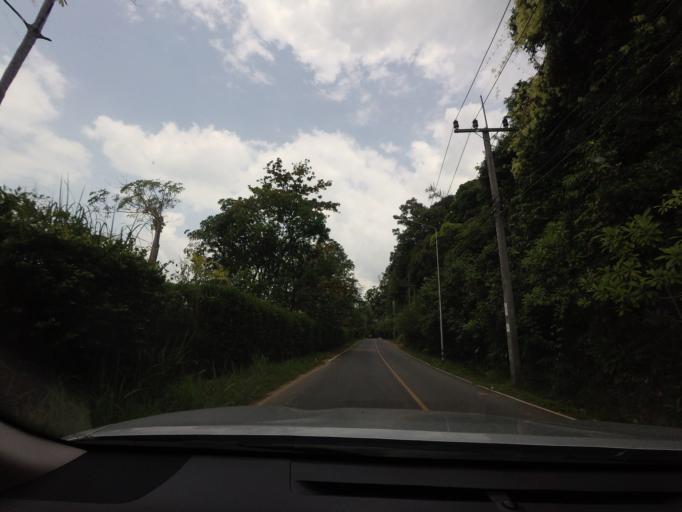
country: TH
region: Phangnga
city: Ban Ao Nang
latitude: 8.0899
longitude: 98.7478
